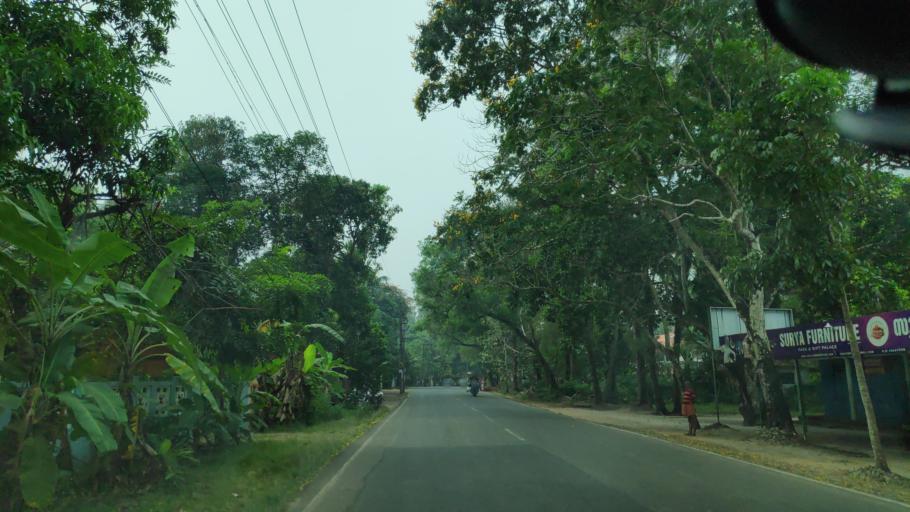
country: IN
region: Kerala
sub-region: Alappuzha
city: Alleppey
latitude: 9.5821
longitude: 76.3506
